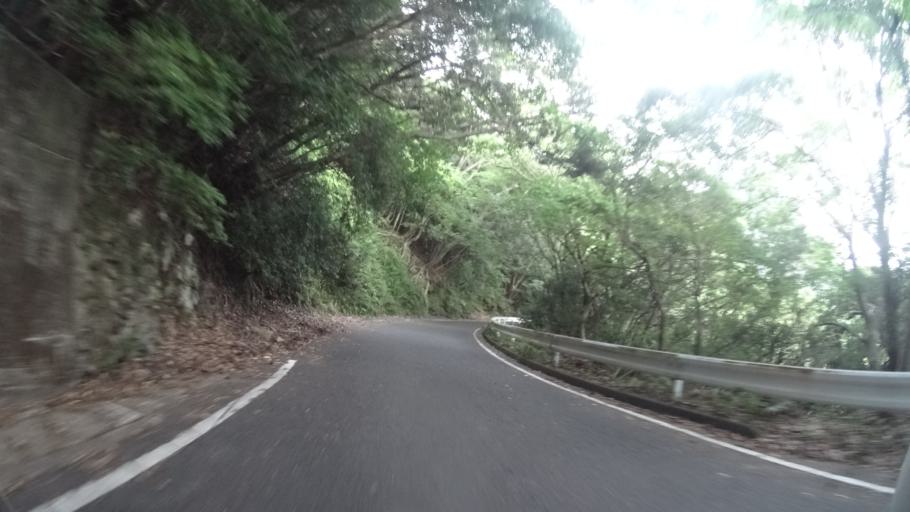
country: JP
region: Kagoshima
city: Nishinoomote
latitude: 30.3348
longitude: 130.3955
